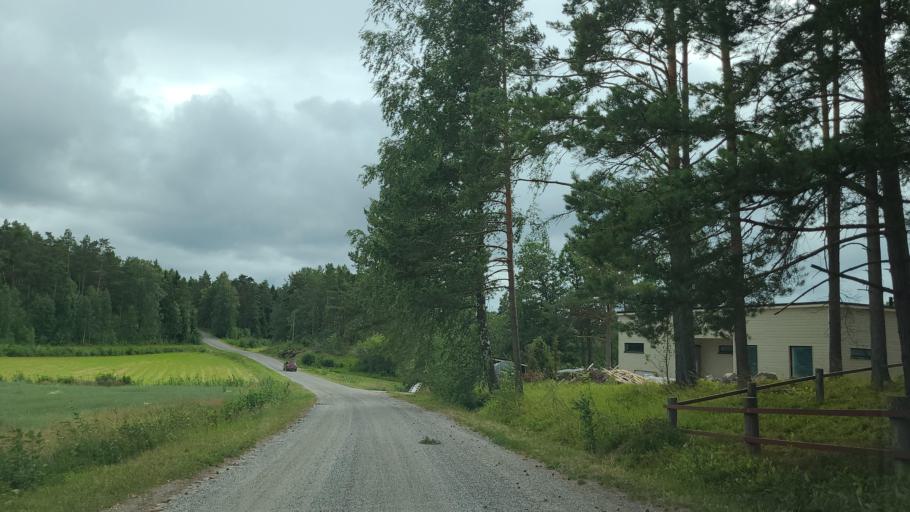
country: FI
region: Varsinais-Suomi
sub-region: Aboland-Turunmaa
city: Dragsfjaerd
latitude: 60.0926
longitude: 22.4163
